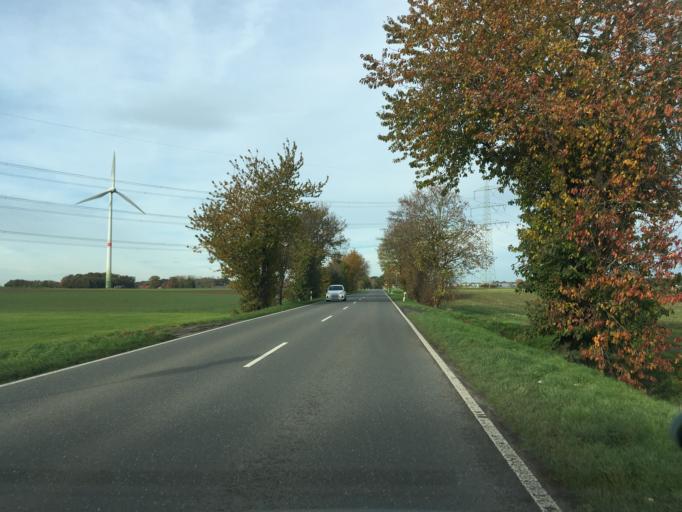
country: DE
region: North Rhine-Westphalia
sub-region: Regierungsbezirk Munster
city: Heiden
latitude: 51.8039
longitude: 6.9520
